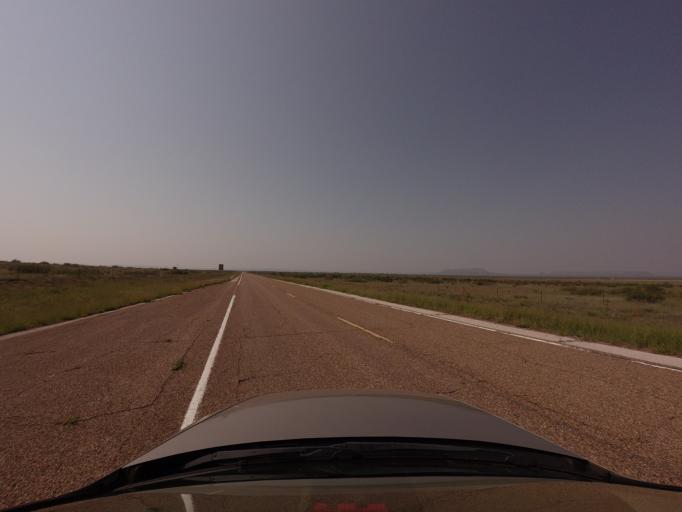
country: US
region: New Mexico
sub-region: Quay County
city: Tucumcari
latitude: 34.9900
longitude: -103.7471
